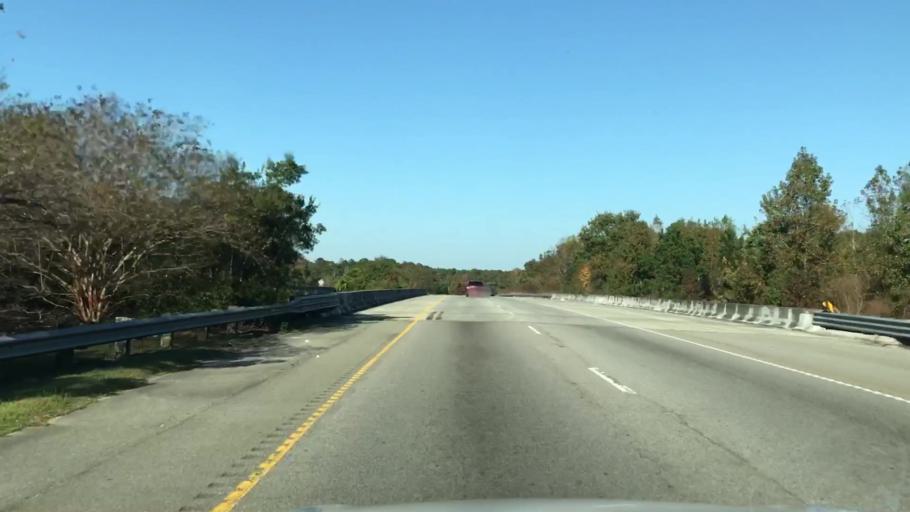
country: US
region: South Carolina
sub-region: Charleston County
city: Shell Point
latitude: 32.8232
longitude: -80.0743
